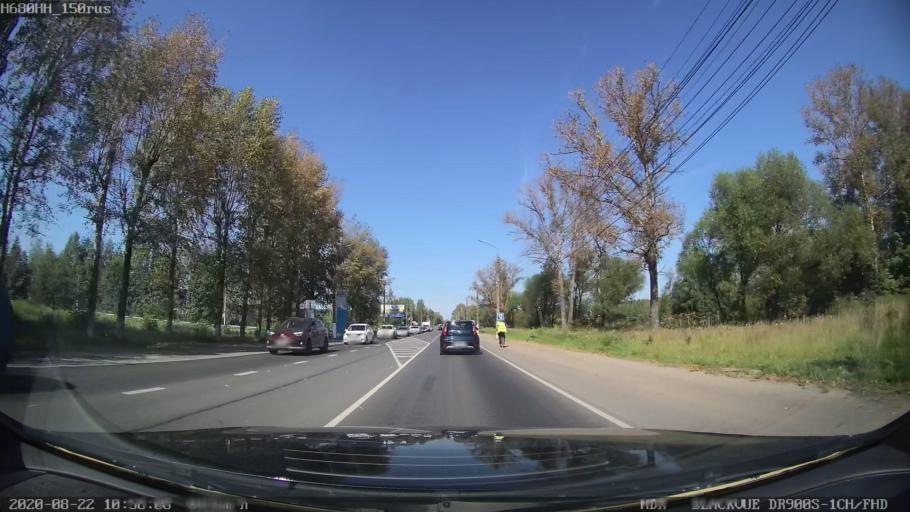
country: RU
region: Tverskaya
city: Tver
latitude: 56.8162
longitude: 35.9878
